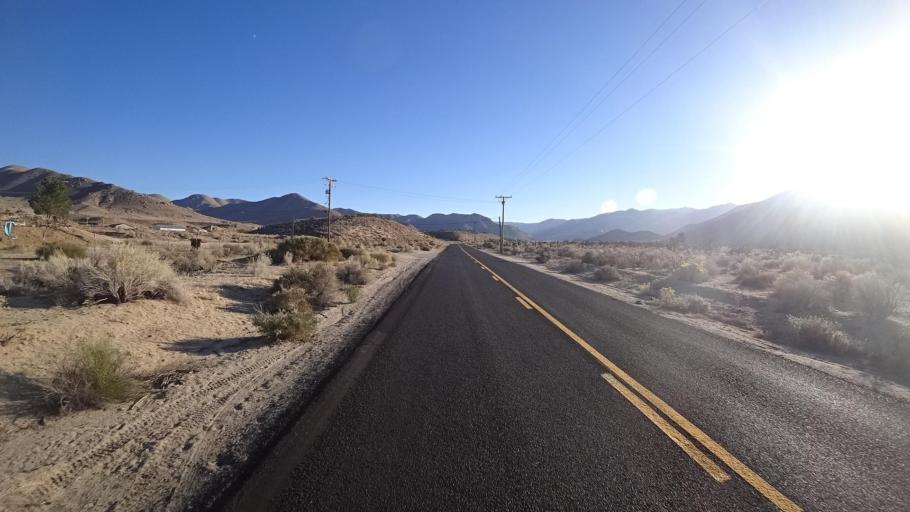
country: US
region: California
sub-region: Kern County
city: Weldon
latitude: 35.6140
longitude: -118.2432
